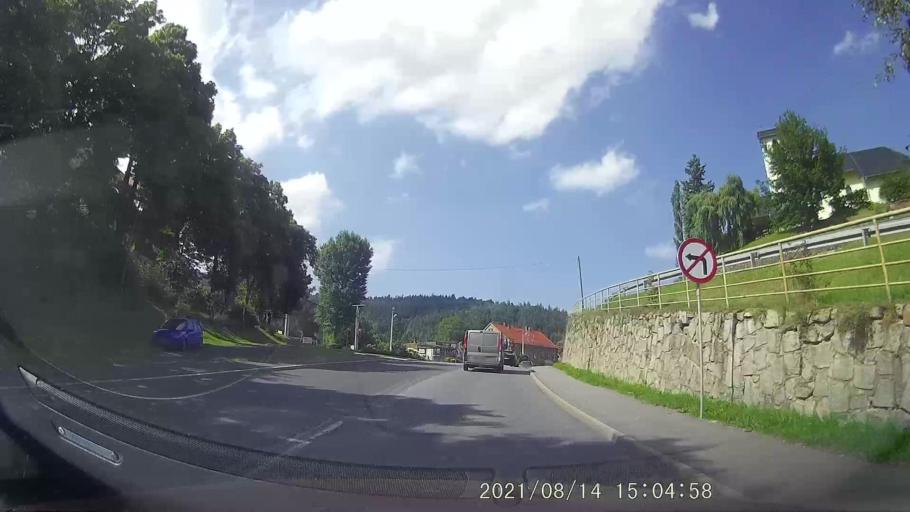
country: PL
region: Lower Silesian Voivodeship
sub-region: Powiat walbrzyski
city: Jedlina-Zdroj
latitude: 50.7356
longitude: 16.3174
